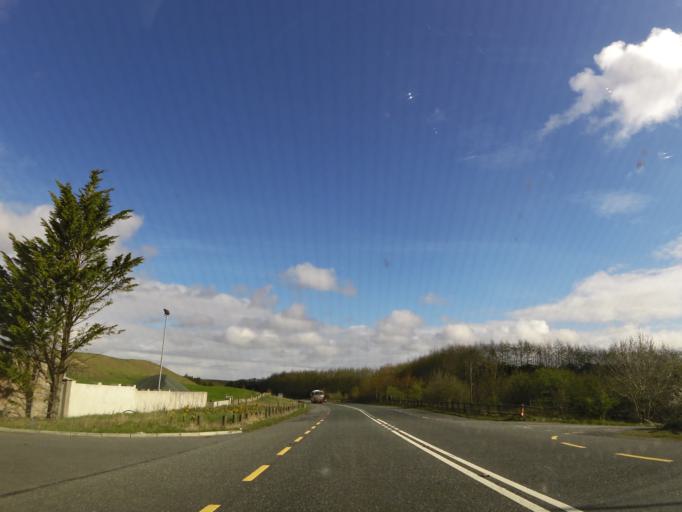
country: IE
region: Connaught
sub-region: Maigh Eo
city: Ballyhaunis
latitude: 53.8573
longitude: -8.8554
